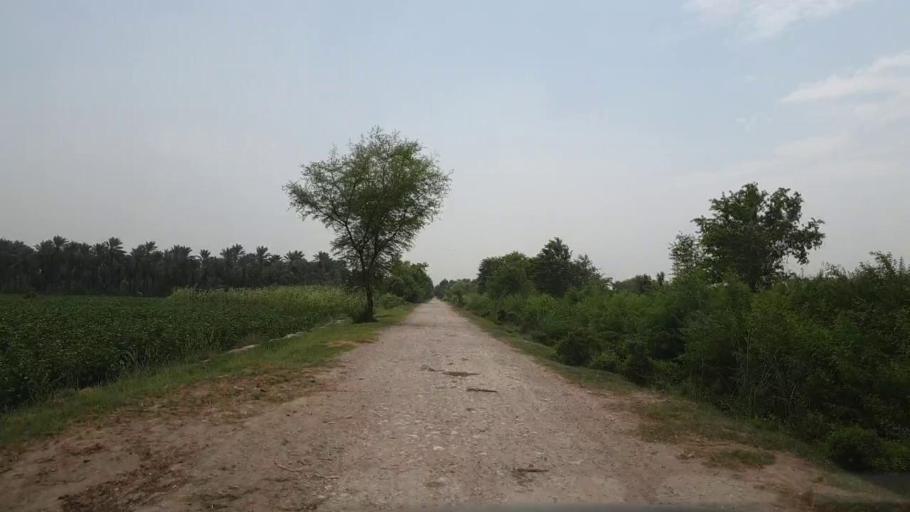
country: PK
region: Sindh
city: Pir jo Goth
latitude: 27.4936
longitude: 68.5984
